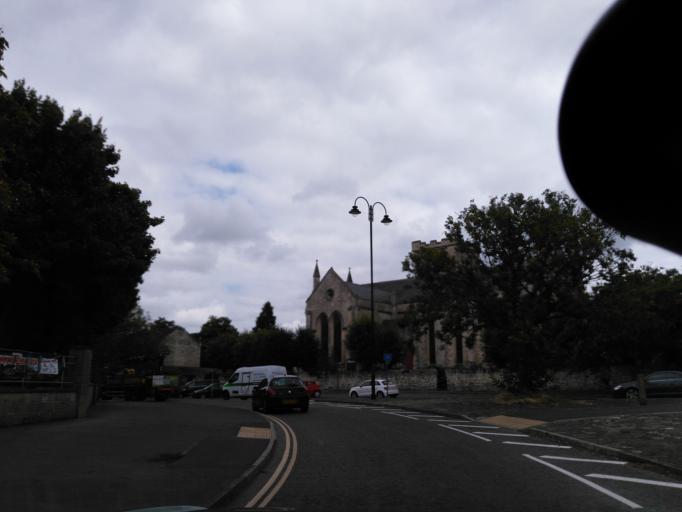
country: GB
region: England
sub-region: Wiltshire
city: Trowbridge
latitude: 51.3188
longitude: -2.2157
